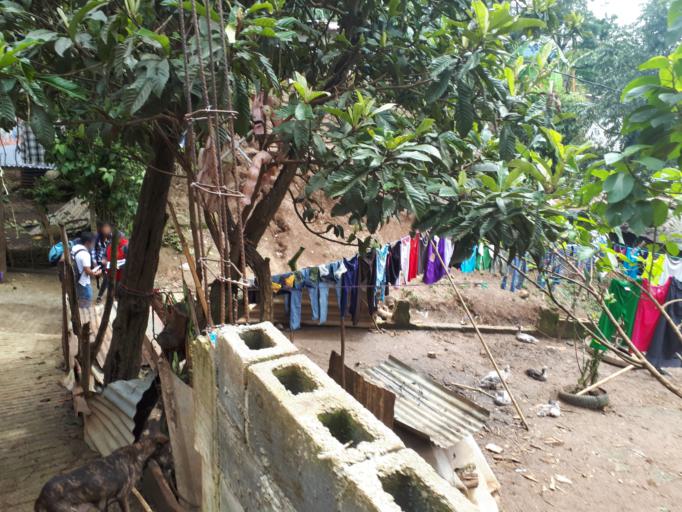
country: GT
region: Guatemala
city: Villa Canales
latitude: 14.4569
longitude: -90.5080
